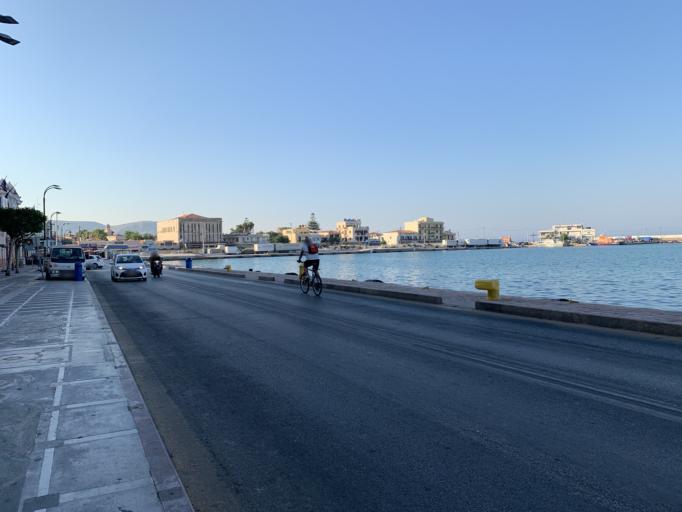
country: GR
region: North Aegean
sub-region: Chios
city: Chios
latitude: 38.3705
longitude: 26.1377
